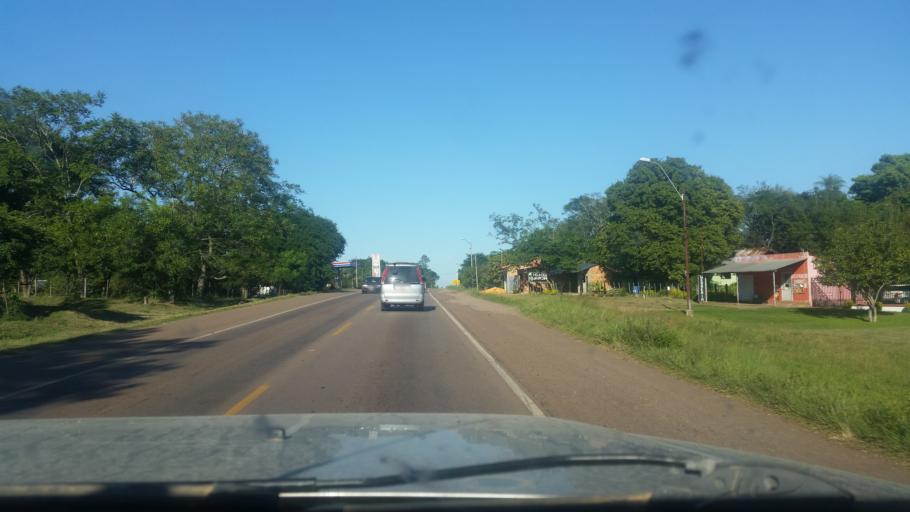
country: PY
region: Paraguari
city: Sapucai
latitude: -25.6646
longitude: -56.9632
